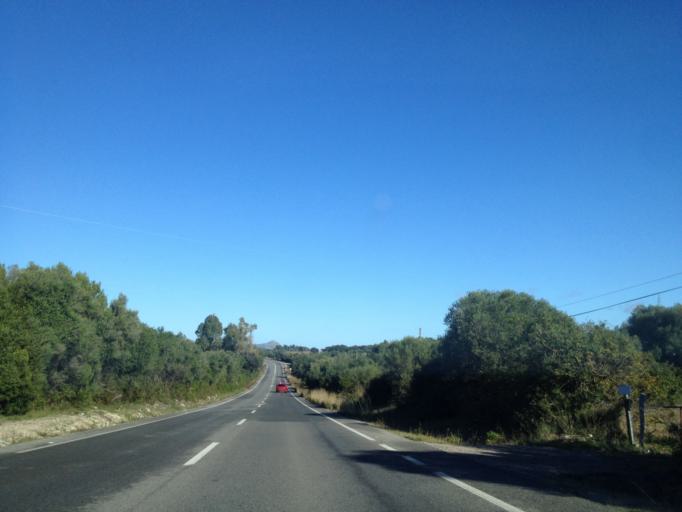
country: ES
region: Balearic Islands
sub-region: Illes Balears
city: Sant Llorenc des Cardassar
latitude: 39.6518
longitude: 3.3158
